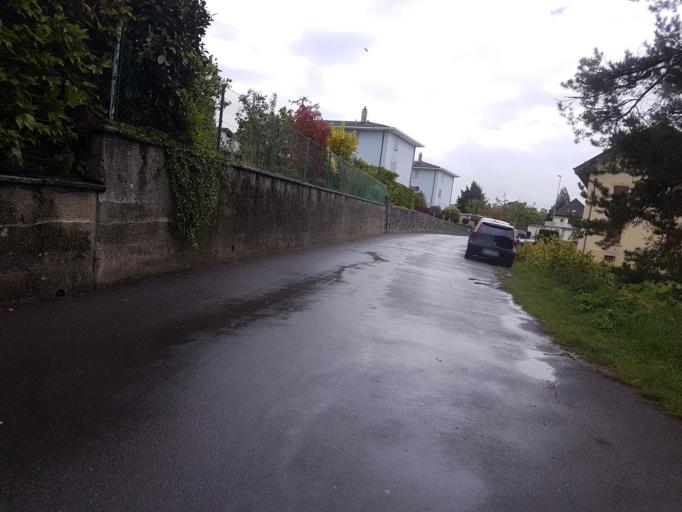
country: CH
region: Vaud
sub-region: Gros-de-Vaud District
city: Penthalaz
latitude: 46.6112
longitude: 6.5214
